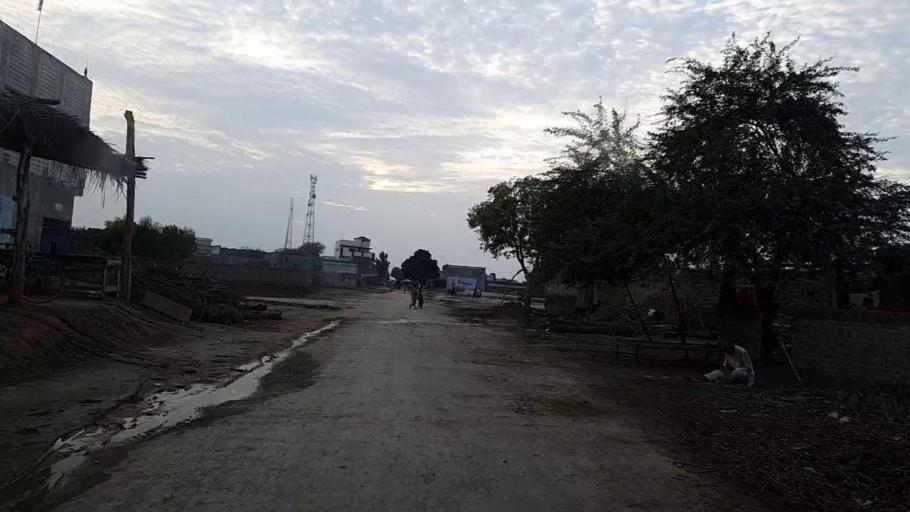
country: PK
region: Sindh
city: Naushahro Firoz
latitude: 26.8094
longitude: 68.2004
